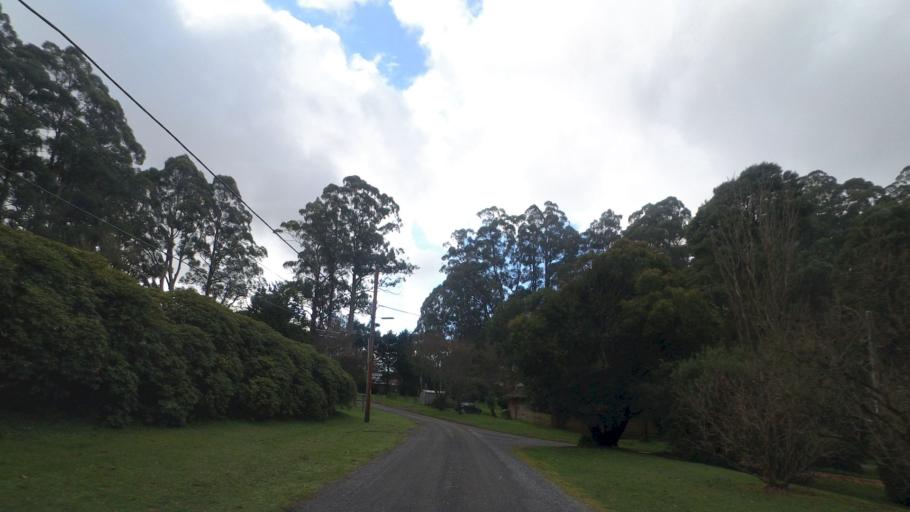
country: AU
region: Victoria
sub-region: Yarra Ranges
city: Olinda
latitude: -37.8455
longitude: 145.3551
